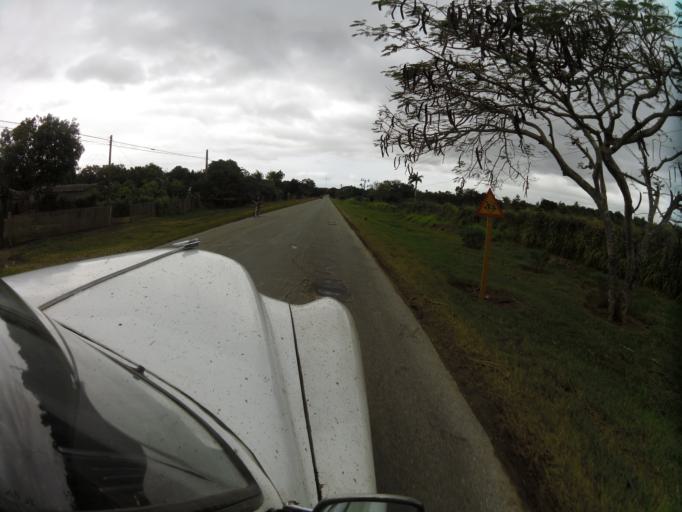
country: CU
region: Las Tunas
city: Las Tunas
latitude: 20.9299
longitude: -76.9107
